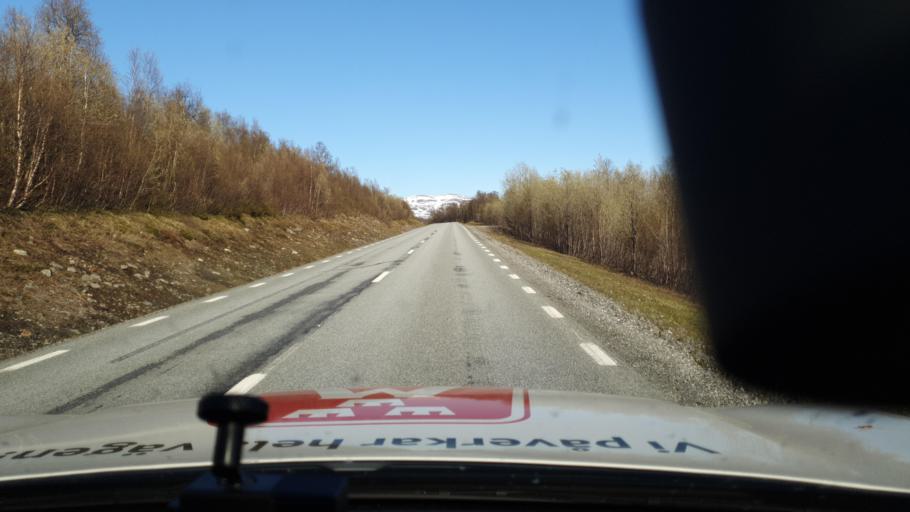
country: NO
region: Nordland
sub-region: Rana
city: Mo i Rana
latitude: 66.0497
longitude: 14.9452
